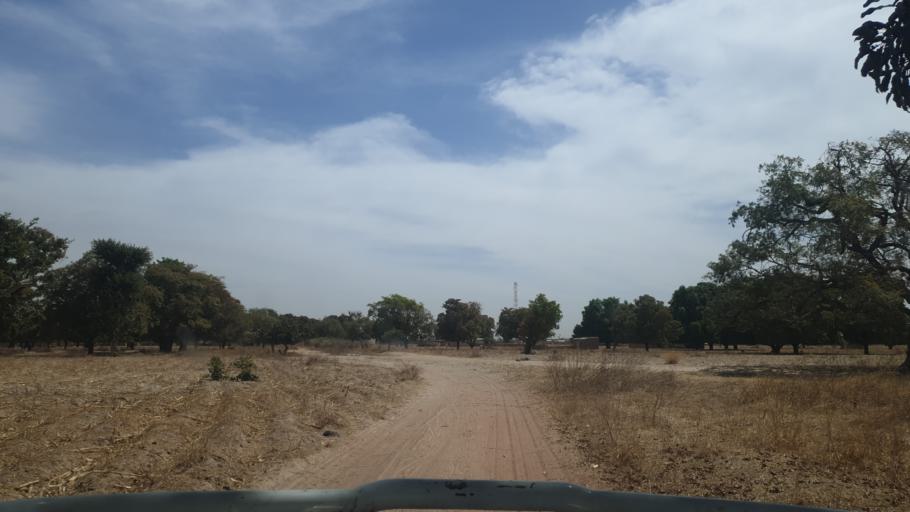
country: ML
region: Sikasso
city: Yorosso
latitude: 12.2916
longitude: -4.6599
